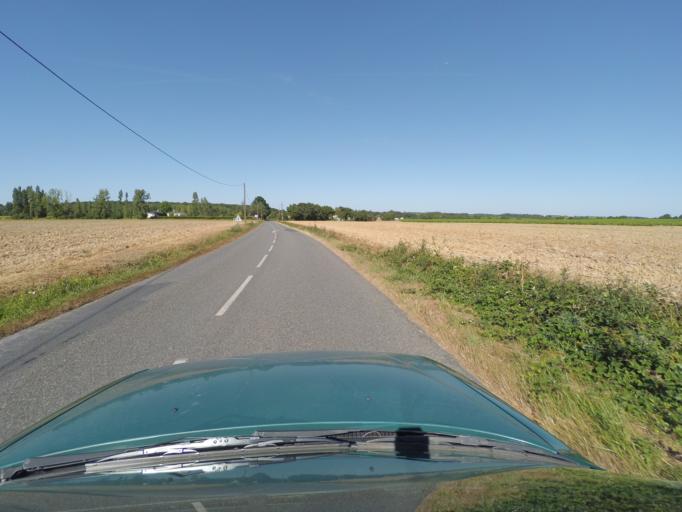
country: FR
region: Pays de la Loire
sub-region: Departement de la Loire-Atlantique
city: Saint-Fiacre-sur-Maine
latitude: 47.1127
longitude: -1.4336
